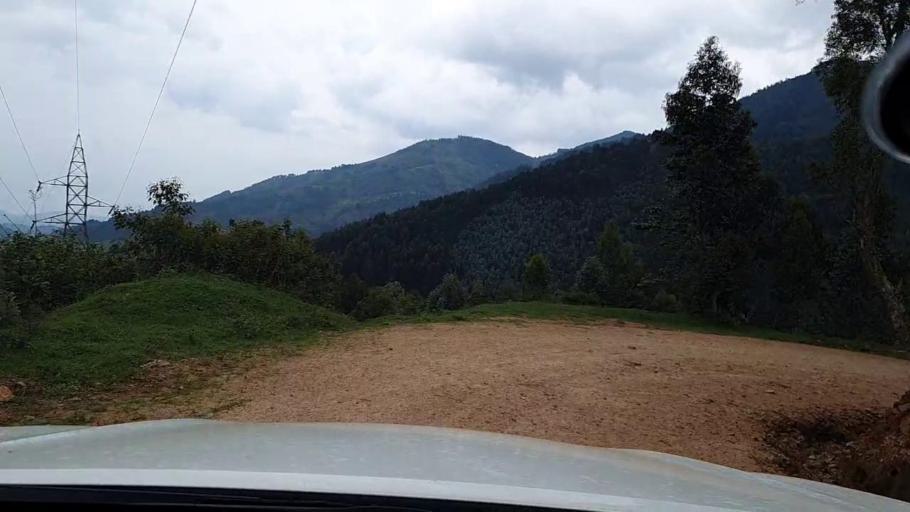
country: RW
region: Western Province
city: Kibuye
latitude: -2.2829
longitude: 29.3015
